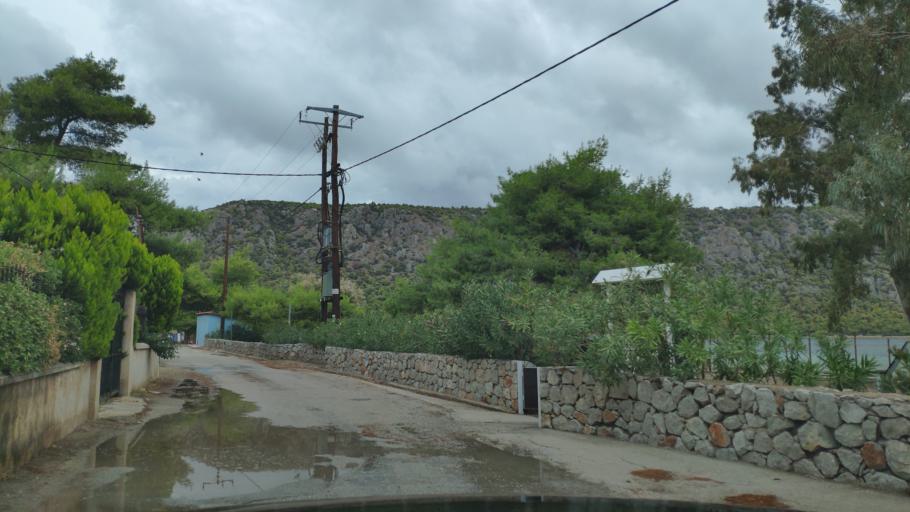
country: GR
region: Peloponnese
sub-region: Nomos Korinthias
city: Perachora
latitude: 38.0269
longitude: 22.8722
